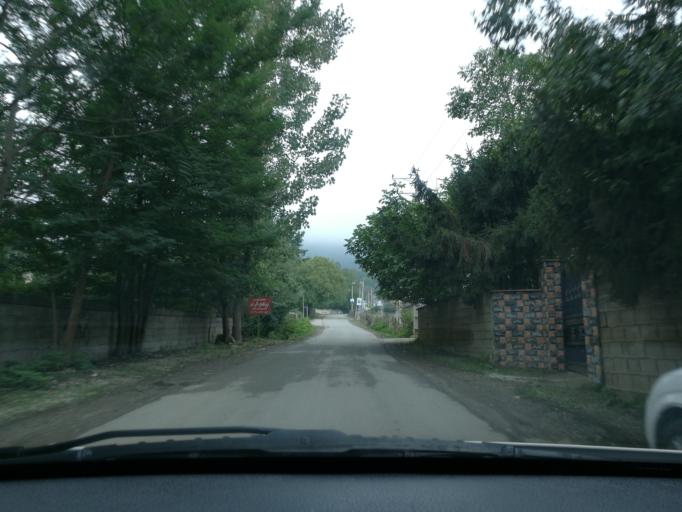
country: IR
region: Mazandaran
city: `Abbasabad
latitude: 36.4999
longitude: 51.2129
